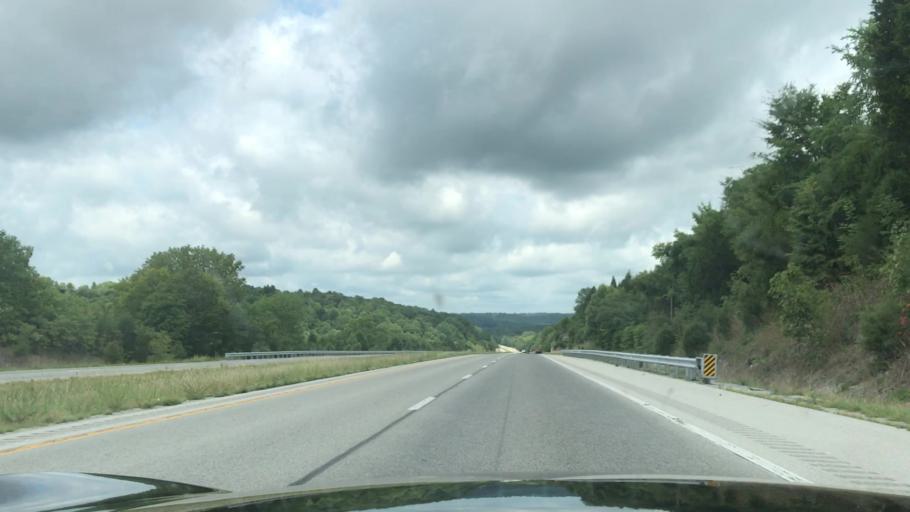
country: US
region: Kentucky
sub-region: Warren County
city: Bowling Green
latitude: 37.0359
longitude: -86.5494
